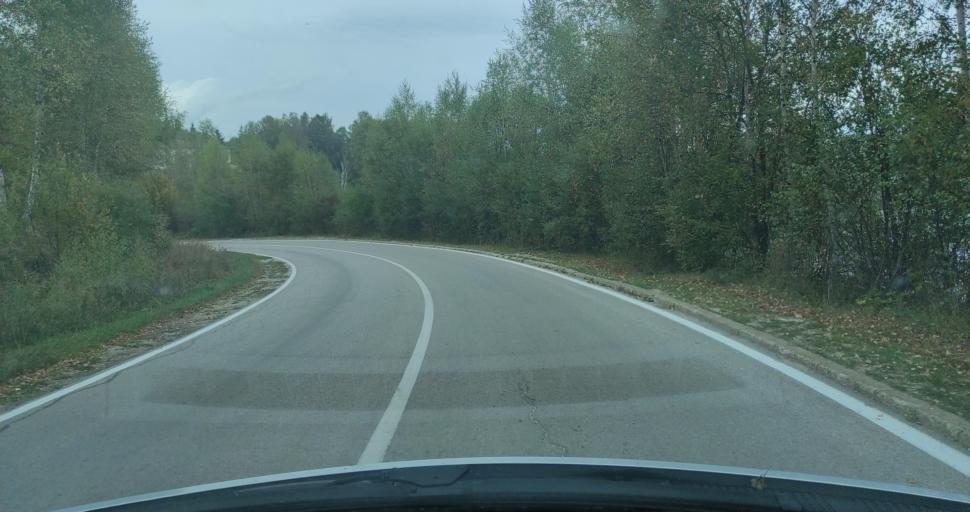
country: RS
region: Central Serbia
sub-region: Jablanicki Okrug
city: Crna Trava
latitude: 42.7375
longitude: 22.3306
